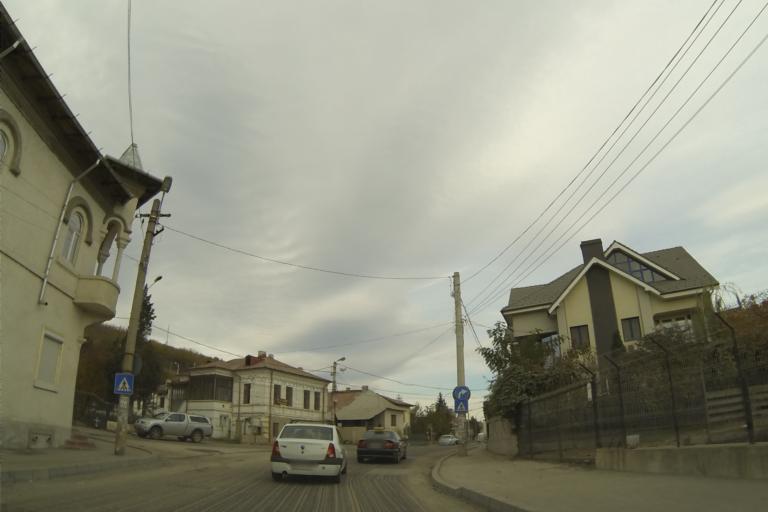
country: RO
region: Olt
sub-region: Municipiul Slatina
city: Slatina
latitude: 44.4258
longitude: 24.3528
